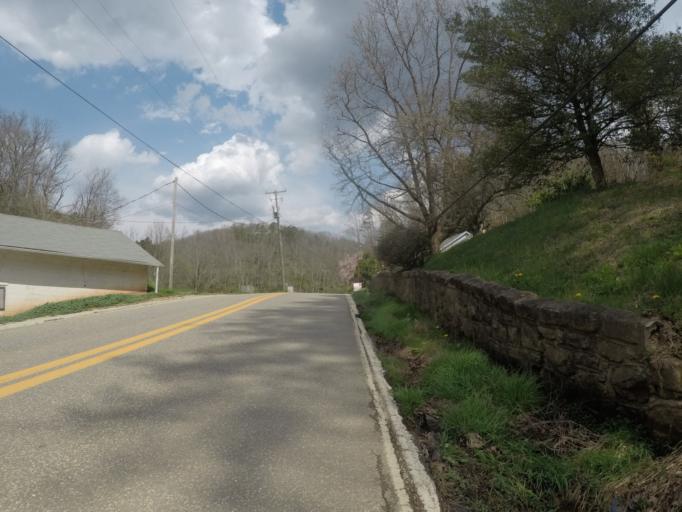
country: US
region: West Virginia
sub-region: Cabell County
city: Pea Ridge
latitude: 38.3434
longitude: -82.3410
